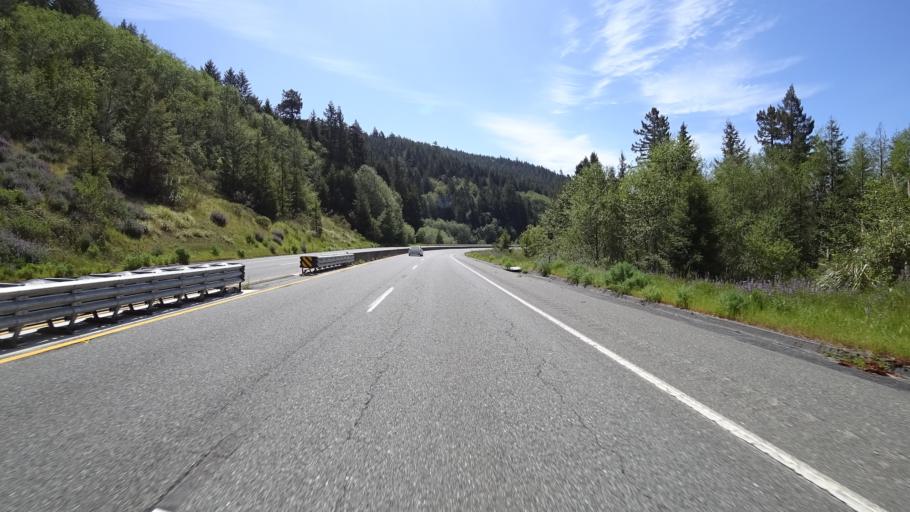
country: US
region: California
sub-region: Humboldt County
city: Westhaven-Moonstone
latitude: 41.3662
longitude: -123.9905
